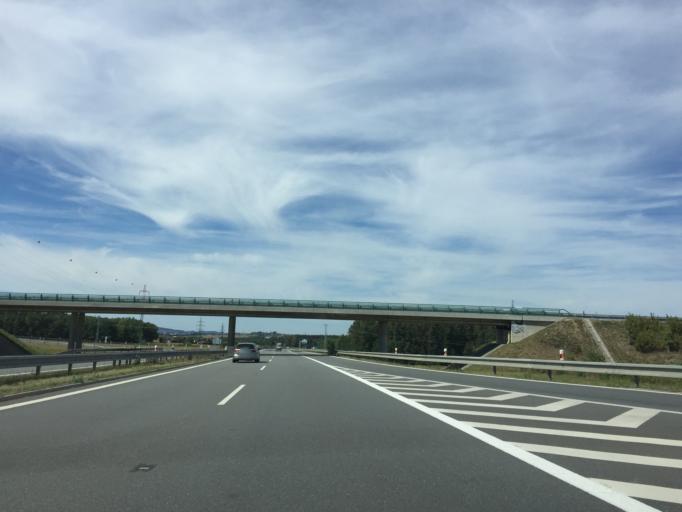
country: CZ
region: Jihocesky
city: Plana nad Luznici
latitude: 49.3662
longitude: 14.7227
